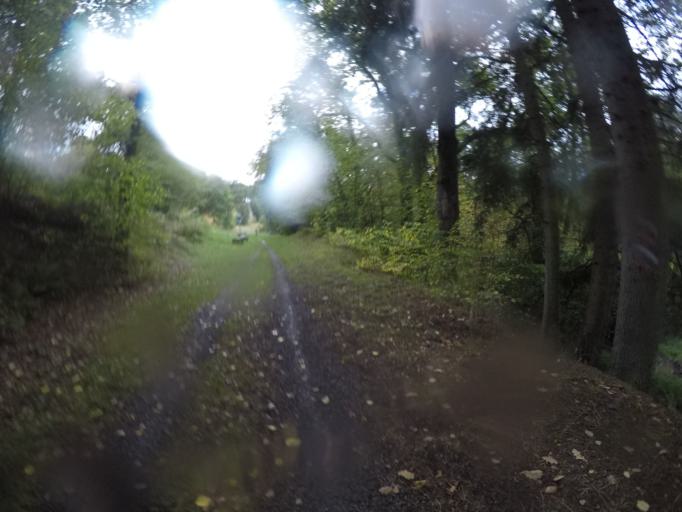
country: BE
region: Wallonia
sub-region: Province du Luxembourg
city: Fauvillers
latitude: 49.8732
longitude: 5.6856
